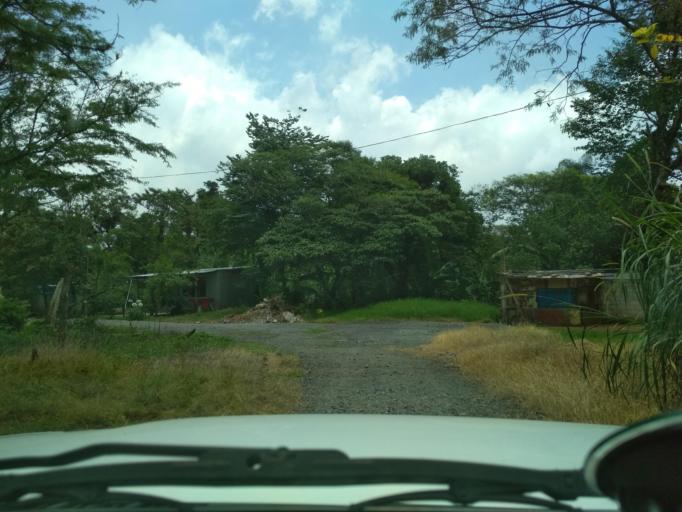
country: MX
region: Veracruz
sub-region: Ixtaczoquitlan
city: Buenavista
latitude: 18.8865
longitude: -97.0627
